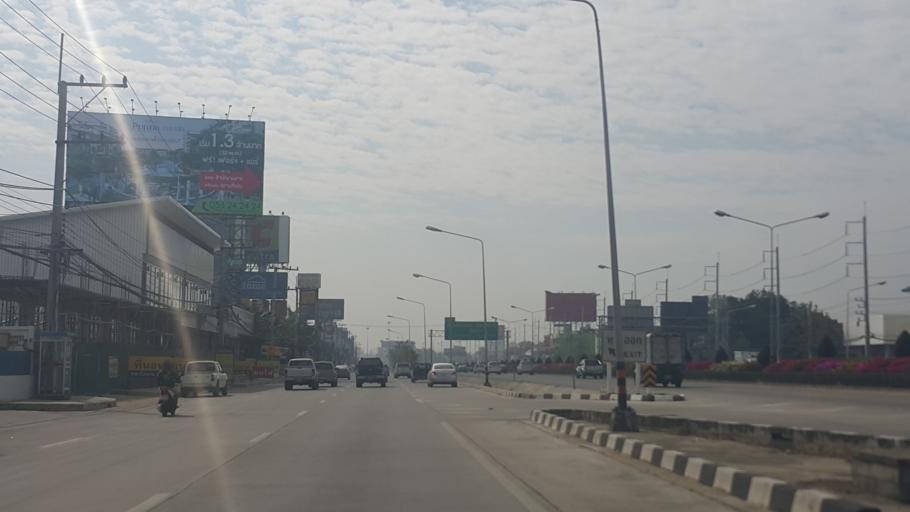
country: TH
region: Chiang Mai
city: Chiang Mai
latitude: 18.7992
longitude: 99.0205
